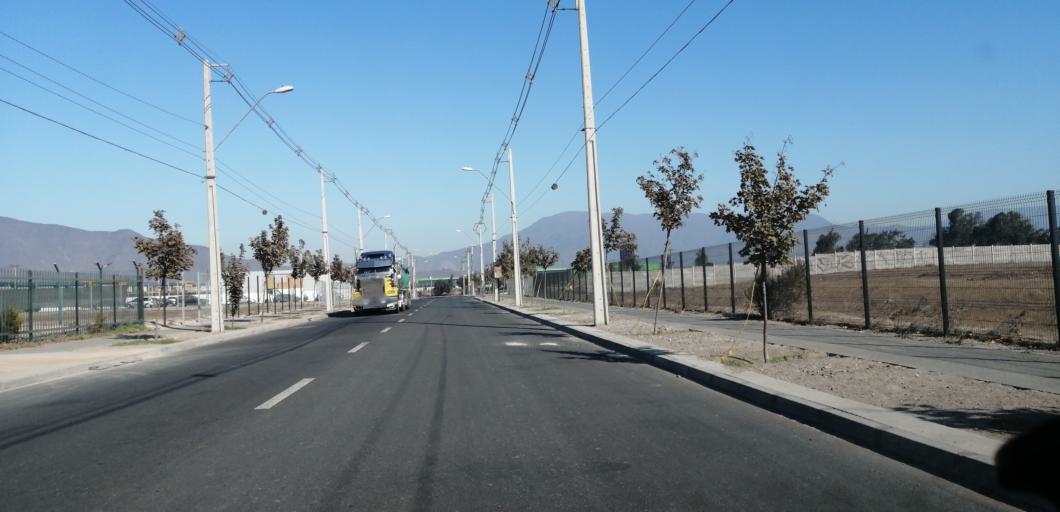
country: CL
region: Santiago Metropolitan
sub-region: Provincia de Santiago
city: Lo Prado
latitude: -33.4431
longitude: -70.7771
